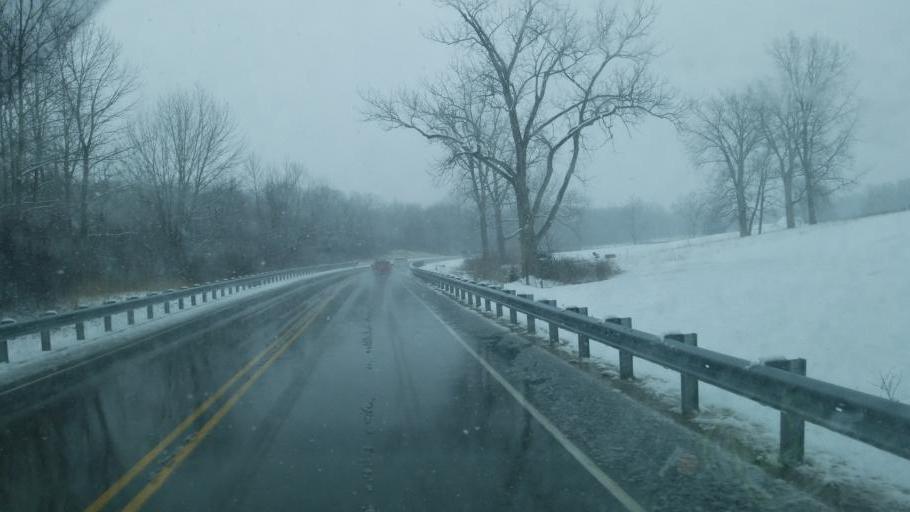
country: US
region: Indiana
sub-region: Wayne County
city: Hagerstown
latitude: 40.0021
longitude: -85.1621
